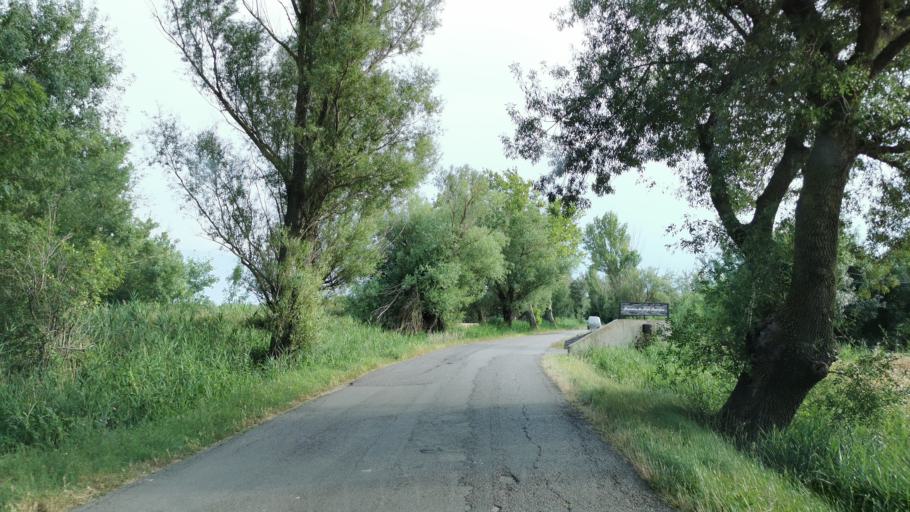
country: FR
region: Languedoc-Roussillon
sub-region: Departement de l'Aude
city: Narbonne
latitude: 43.2019
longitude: 2.9987
